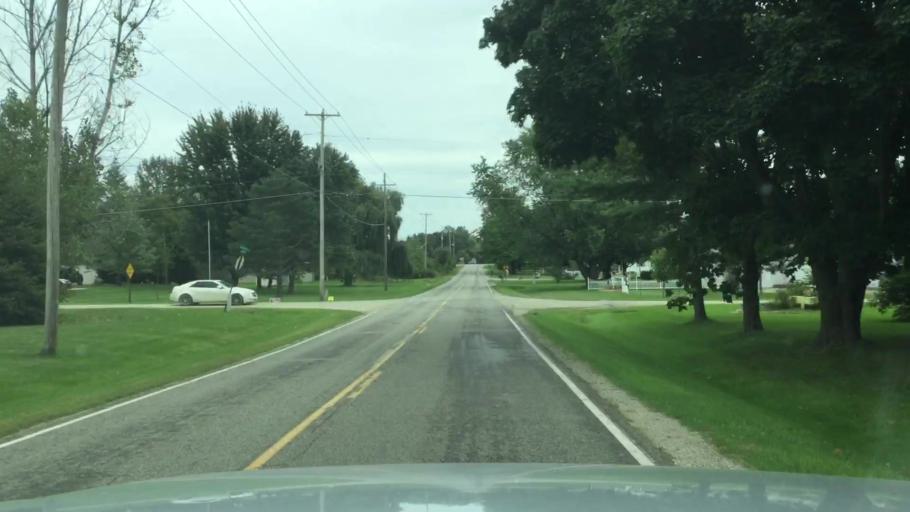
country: US
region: Michigan
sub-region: Shiawassee County
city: Durand
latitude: 42.9516
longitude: -83.9343
